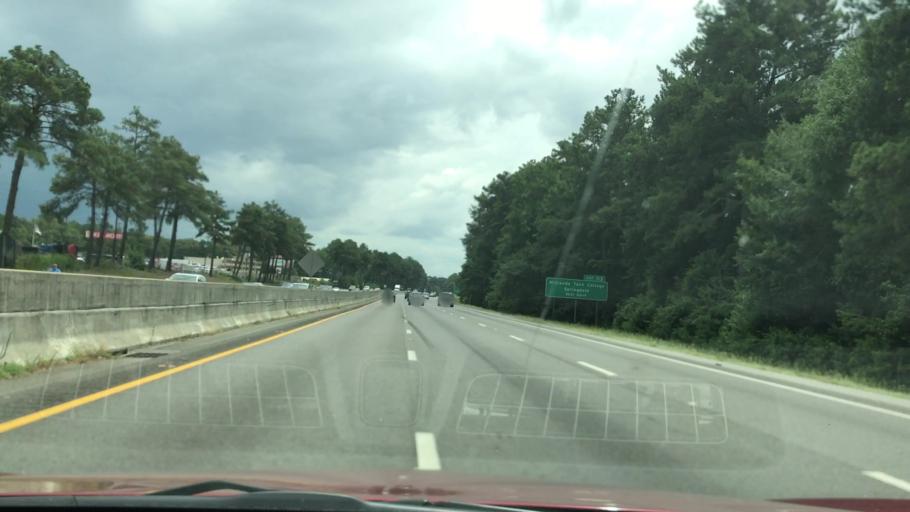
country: US
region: South Carolina
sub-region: Lexington County
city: Springdale
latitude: 33.9632
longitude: -81.0968
